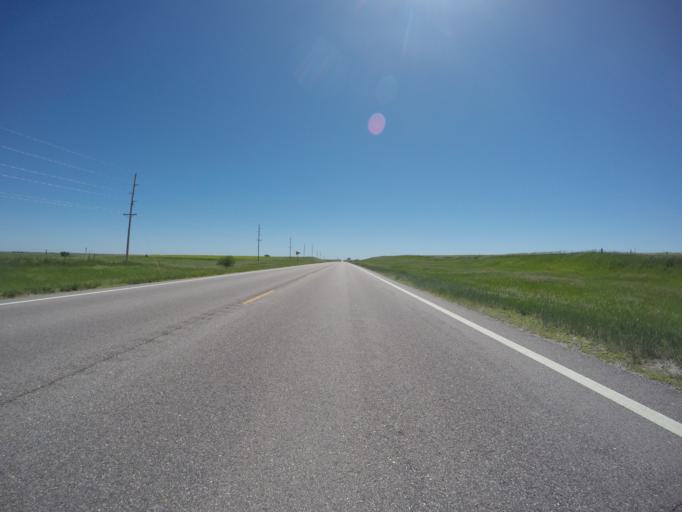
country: US
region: Kansas
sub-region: Norton County
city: Norton
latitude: 39.8284
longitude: -99.6766
